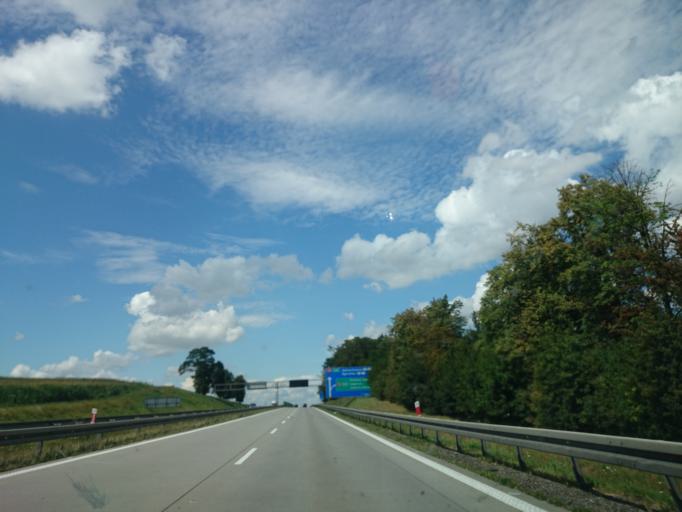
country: PL
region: Lower Silesian Voivodeship
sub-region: Powiat legnicki
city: Legnickie Pole
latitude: 51.1589
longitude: 16.1975
